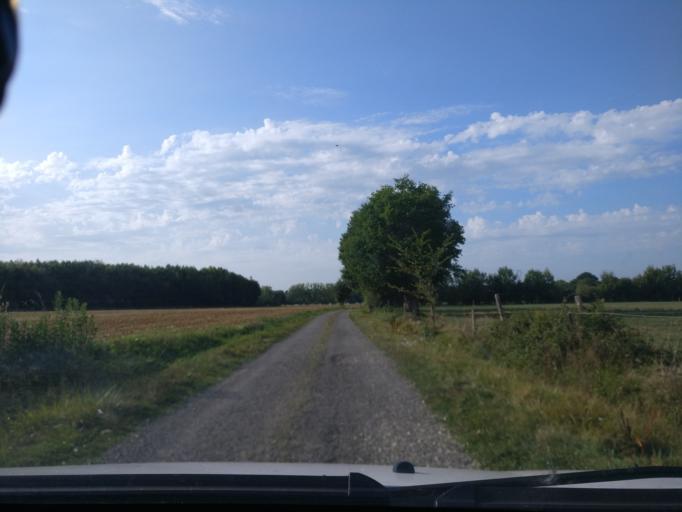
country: FR
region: Brittany
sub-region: Departement d'Ille-et-Vilaine
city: Fouillard
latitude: 48.1342
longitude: -1.5725
